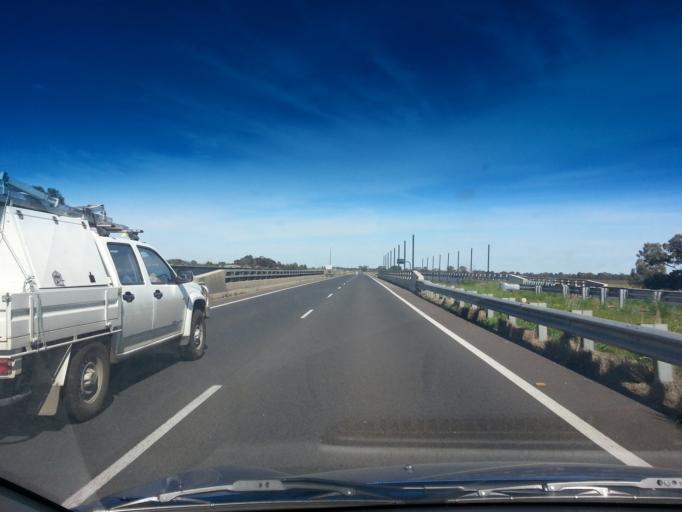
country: AU
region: South Australia
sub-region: Playford
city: Angle Vale
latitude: -34.6152
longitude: 138.6809
